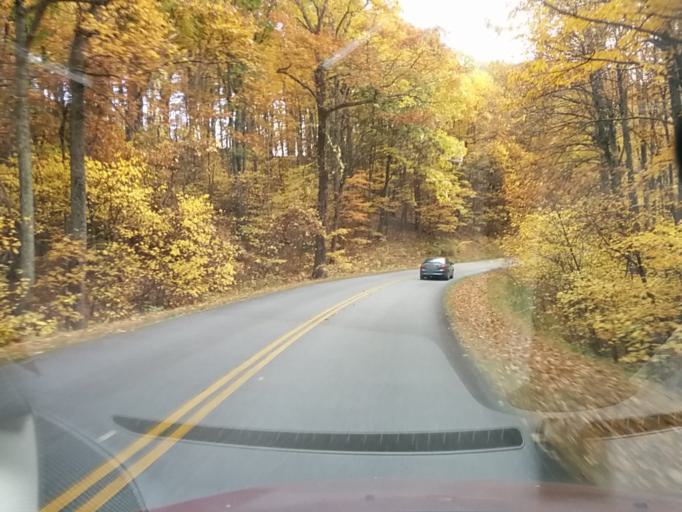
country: US
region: Virginia
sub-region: Augusta County
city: Stuarts Draft
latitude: 37.8451
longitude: -79.1558
